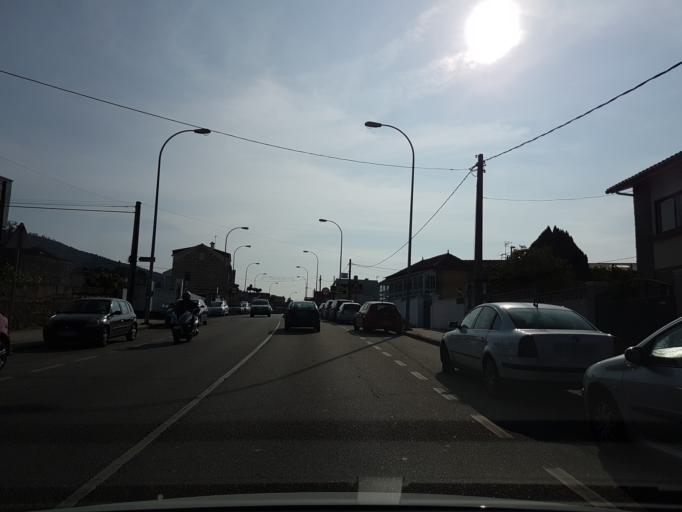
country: ES
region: Galicia
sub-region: Provincia de Pontevedra
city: Vigo
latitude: 42.1960
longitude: -8.7666
